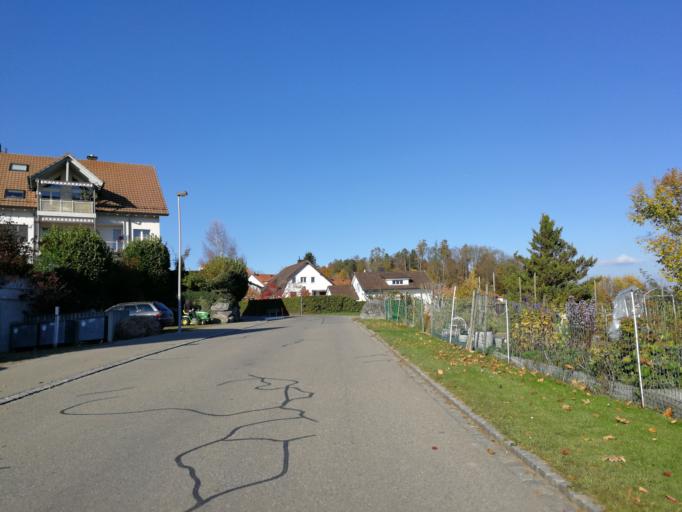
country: CH
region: Zurich
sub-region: Bezirk Uster
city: Egg
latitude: 47.3005
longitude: 8.6946
